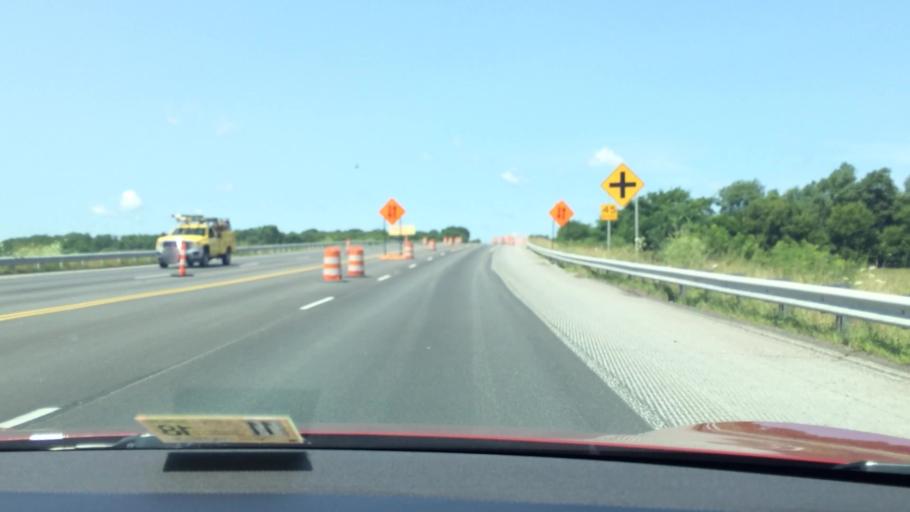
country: US
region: Indiana
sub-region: LaPorte County
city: Hudson Lake
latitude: 41.6701
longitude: -86.6133
